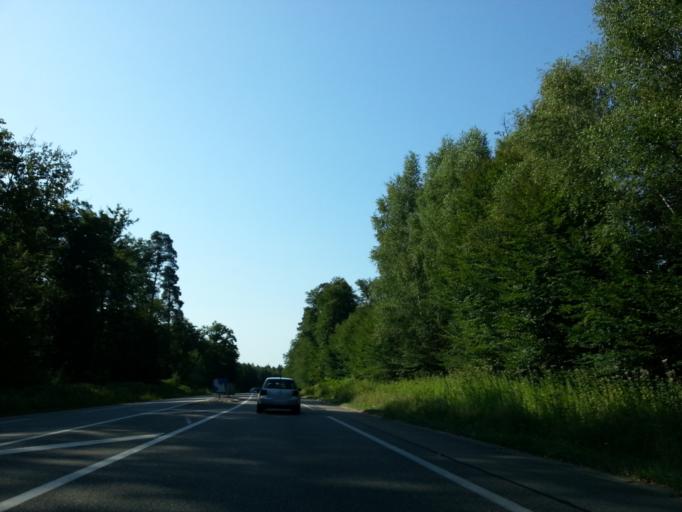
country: FR
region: Alsace
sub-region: Departement du Bas-Rhin
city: Walbourg
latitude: 48.8770
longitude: 7.8254
